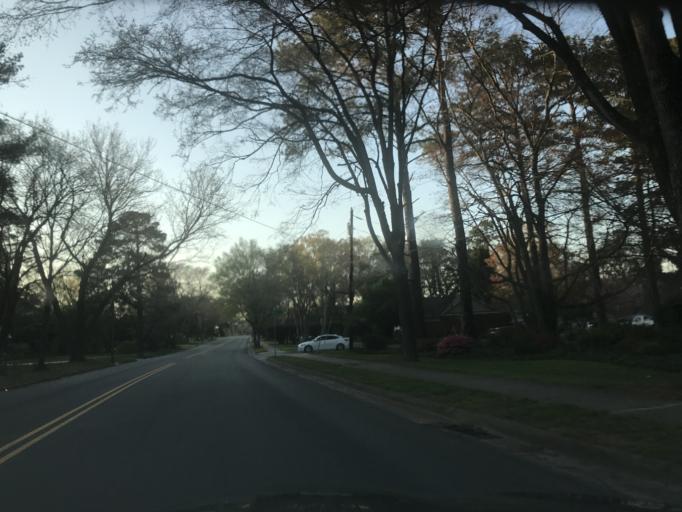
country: US
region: North Carolina
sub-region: Wake County
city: Raleigh
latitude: 35.7765
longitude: -78.6055
